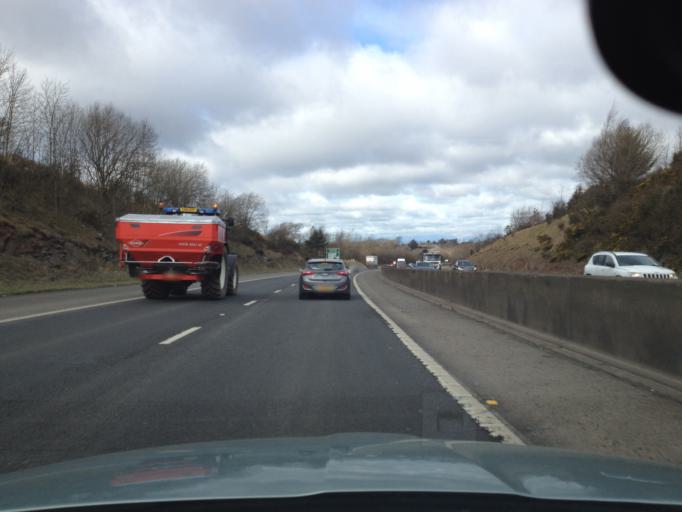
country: GB
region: Scotland
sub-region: Edinburgh
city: Colinton
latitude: 55.9006
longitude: -3.2695
